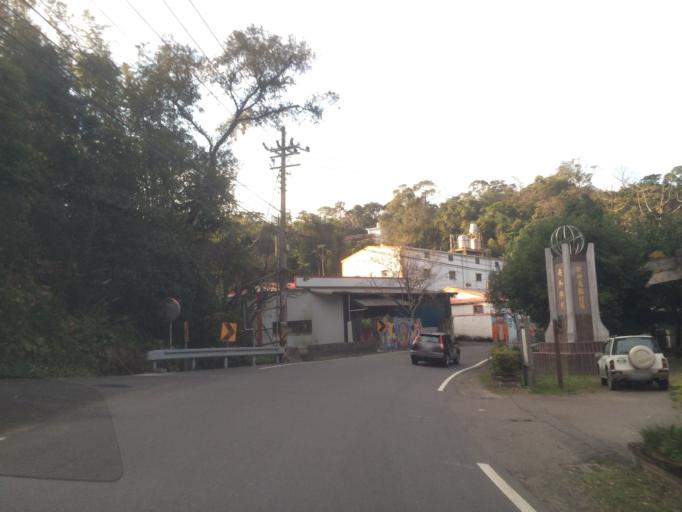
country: TW
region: Taiwan
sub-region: Hsinchu
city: Hsinchu
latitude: 24.6972
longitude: 121.0959
